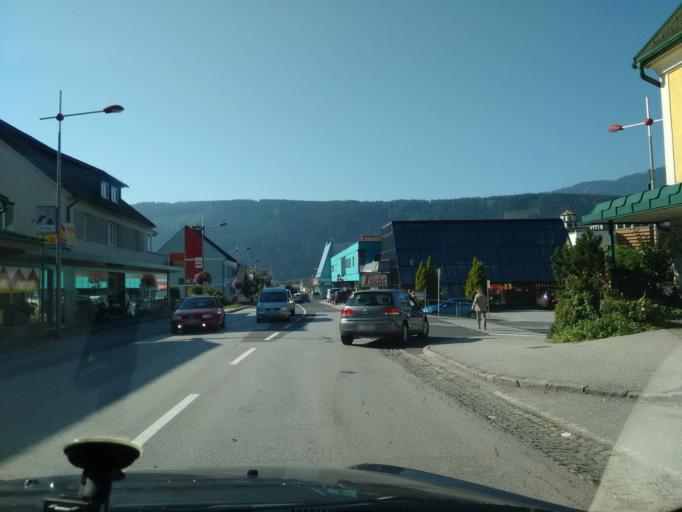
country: AT
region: Styria
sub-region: Politischer Bezirk Liezen
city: Liezen
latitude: 47.5656
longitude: 14.2438
